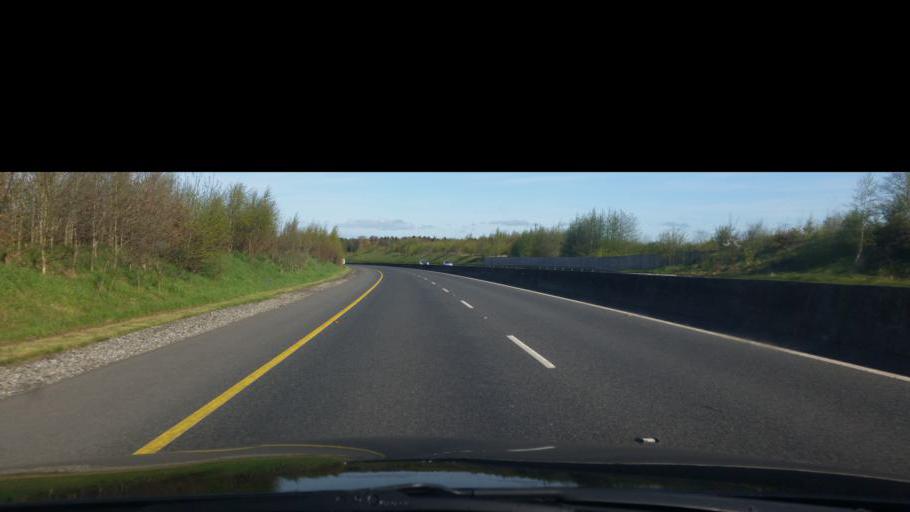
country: IE
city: Kentstown
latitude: 53.5937
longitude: -6.5856
